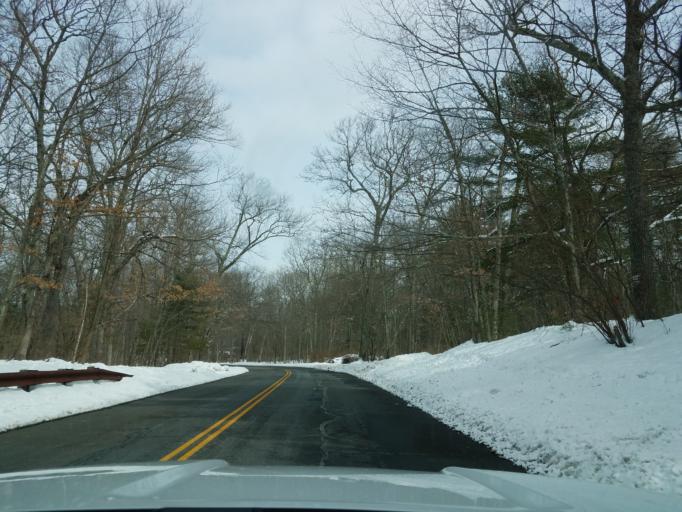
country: US
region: Connecticut
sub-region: Litchfield County
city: Litchfield
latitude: 41.7169
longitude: -73.2217
